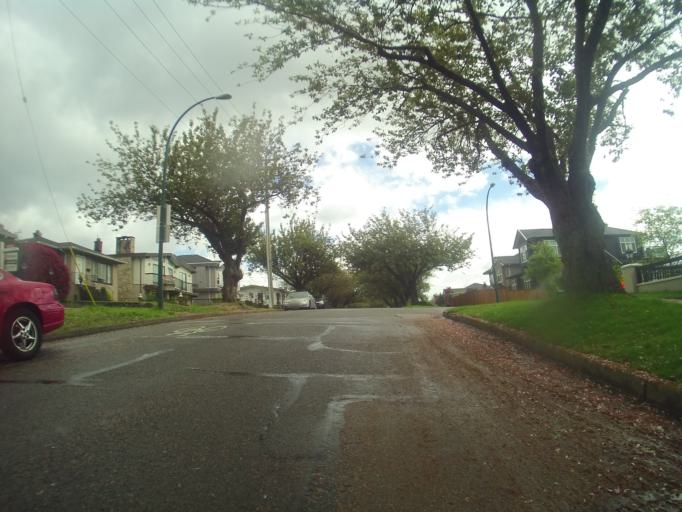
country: CA
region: British Columbia
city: Vancouver
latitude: 49.2440
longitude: -123.0736
